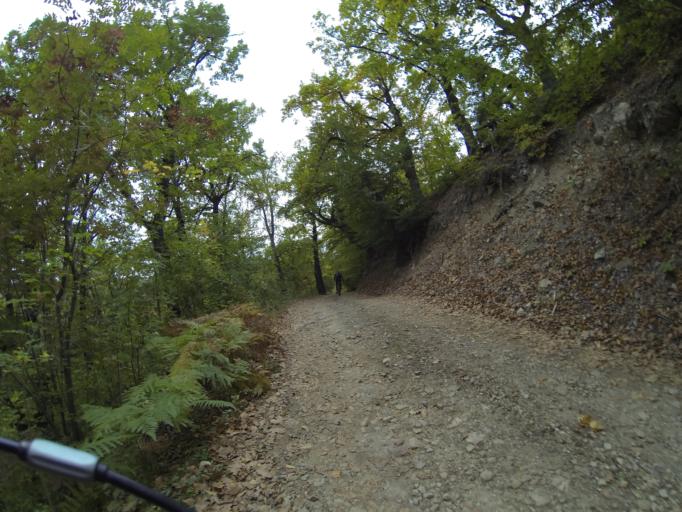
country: RO
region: Gorj
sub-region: Comuna Tismana
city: Sohodol
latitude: 45.0737
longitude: 22.8630
